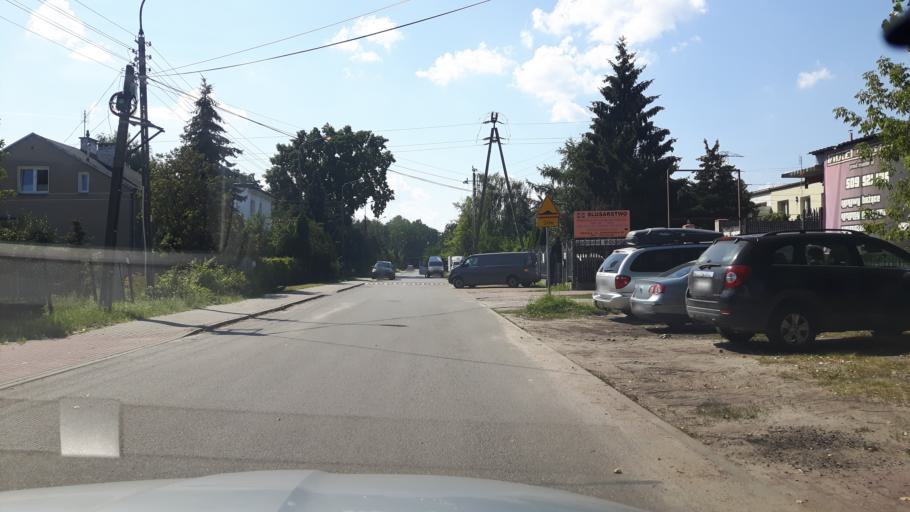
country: PL
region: Masovian Voivodeship
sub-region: Warszawa
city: Rembertow
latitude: 52.2445
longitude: 21.1823
